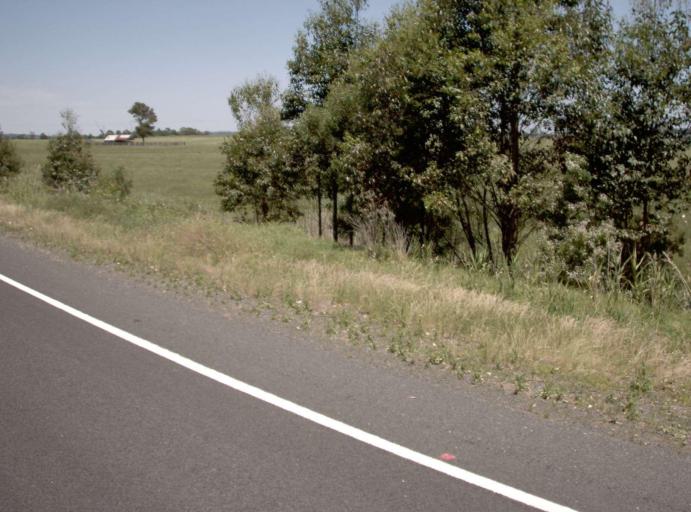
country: AU
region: Victoria
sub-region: East Gippsland
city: Lakes Entrance
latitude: -37.7047
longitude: 148.5403
